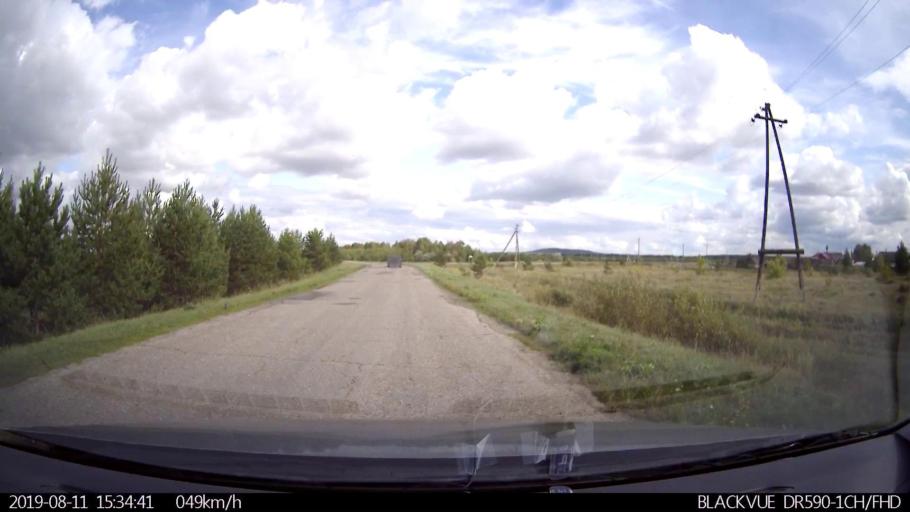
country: RU
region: Ulyanovsk
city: Ignatovka
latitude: 53.8607
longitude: 47.5983
